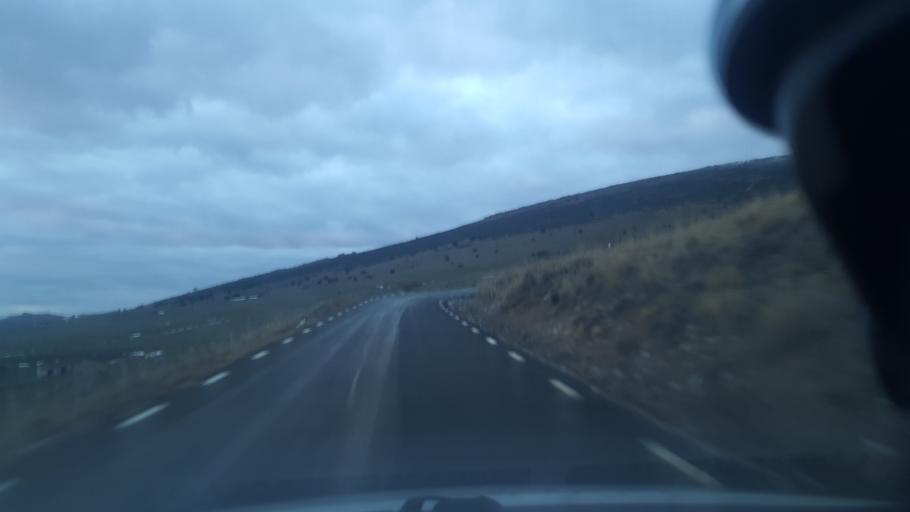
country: ES
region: Castille and Leon
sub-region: Provincia de Avila
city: Ojos-Albos
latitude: 40.7010
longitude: -4.4455
